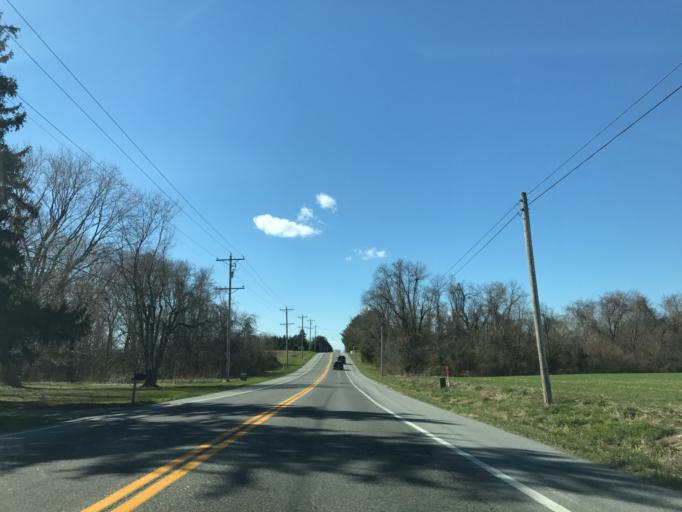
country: US
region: Maryland
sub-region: Kent County
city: Chestertown
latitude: 39.2157
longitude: -76.1188
